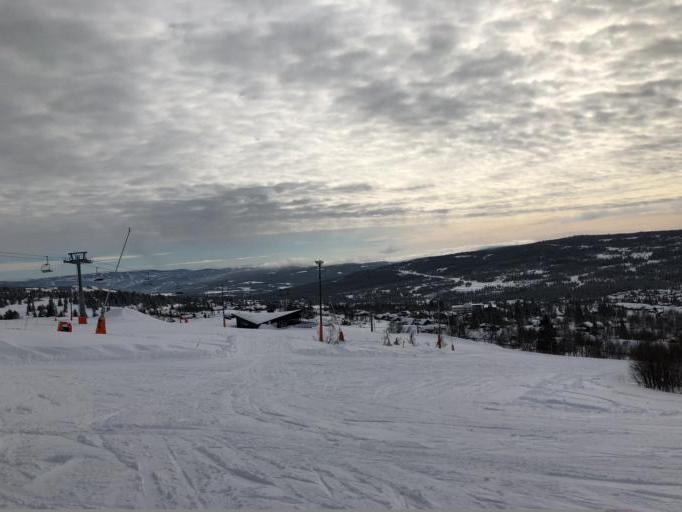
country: NO
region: Oppland
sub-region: Gausdal
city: Segalstad bru
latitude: 61.3431
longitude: 10.0883
